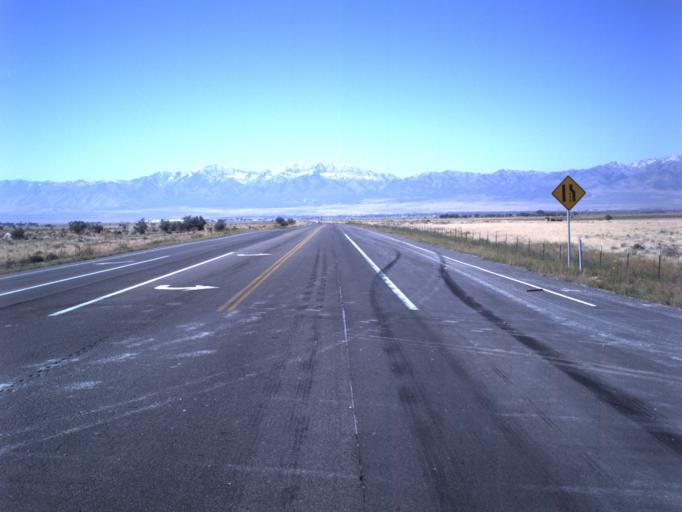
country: US
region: Utah
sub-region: Tooele County
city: Stansbury park
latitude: 40.6373
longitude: -112.3258
